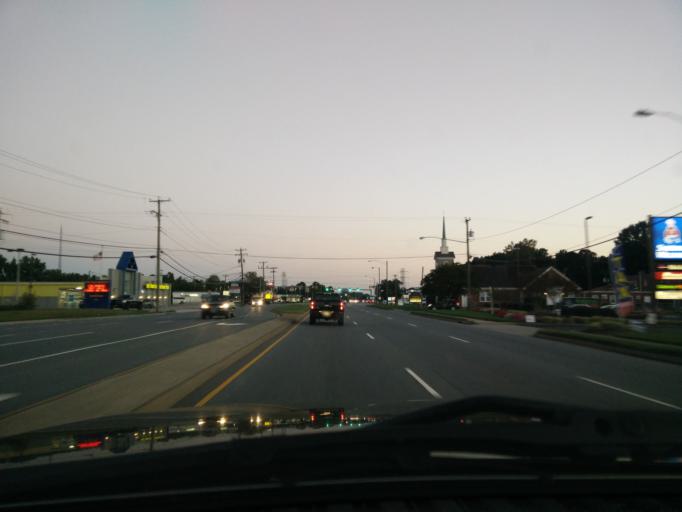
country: US
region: Virginia
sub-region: City of Chesapeake
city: Chesapeake
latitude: 36.7571
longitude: -76.2491
